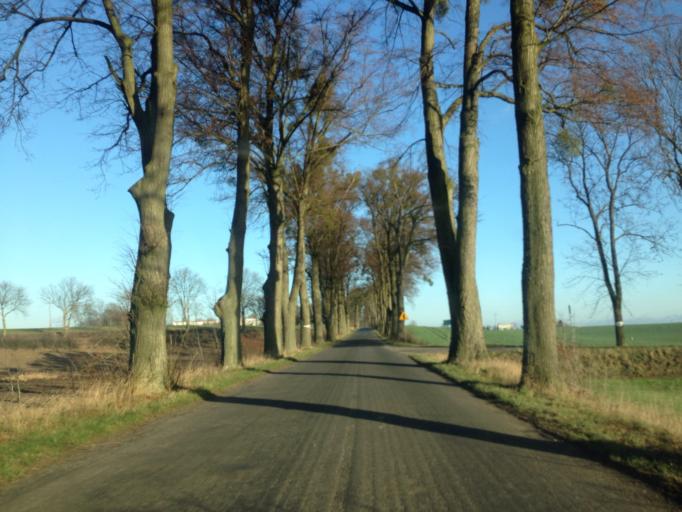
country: PL
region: Kujawsko-Pomorskie
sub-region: Powiat grudziadzki
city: Swiecie nad Osa
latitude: 53.4585
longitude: 19.1528
